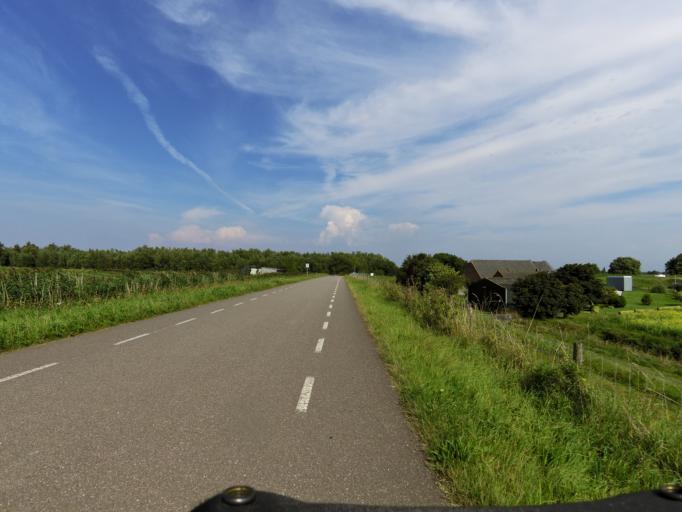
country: NL
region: South Holland
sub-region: Gemeente Zwijndrecht
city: Heerjansdam
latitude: 51.8233
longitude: 4.5518
